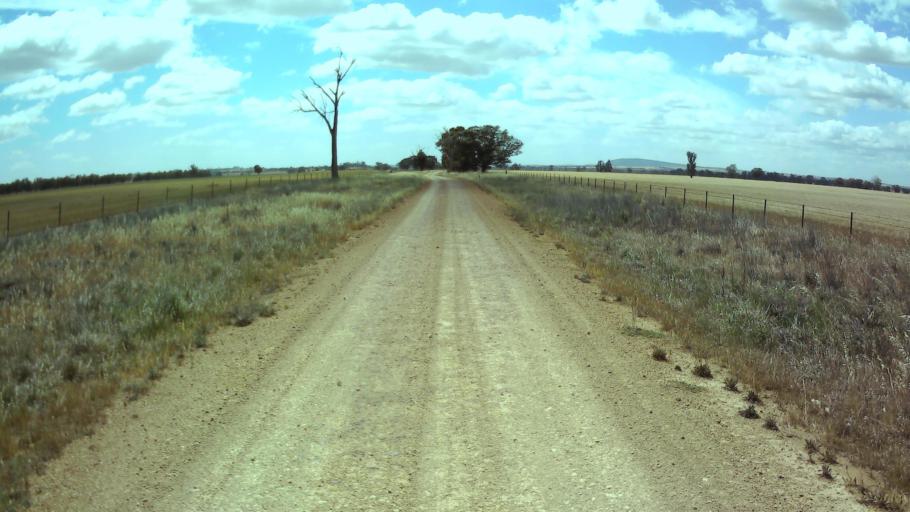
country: AU
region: New South Wales
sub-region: Weddin
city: Grenfell
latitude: -33.9955
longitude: 148.2796
